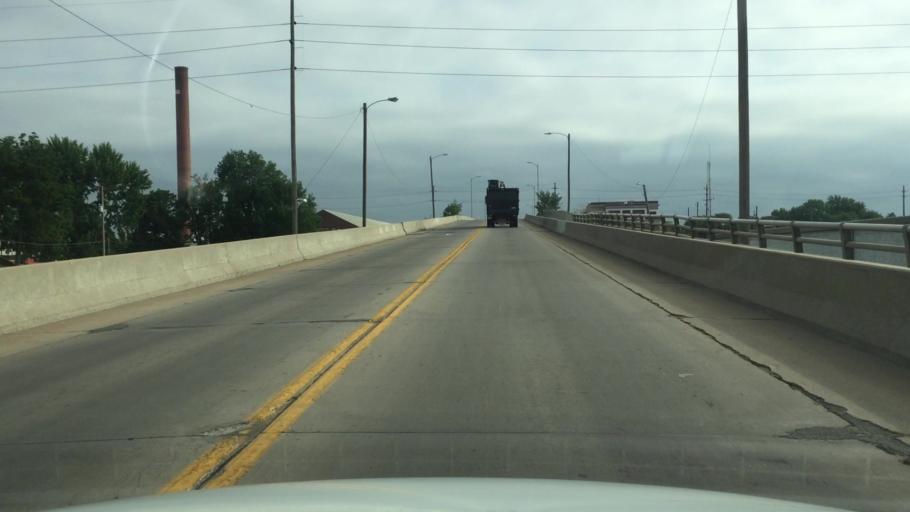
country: US
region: Kansas
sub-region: Shawnee County
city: Topeka
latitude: 39.0536
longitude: -95.6589
